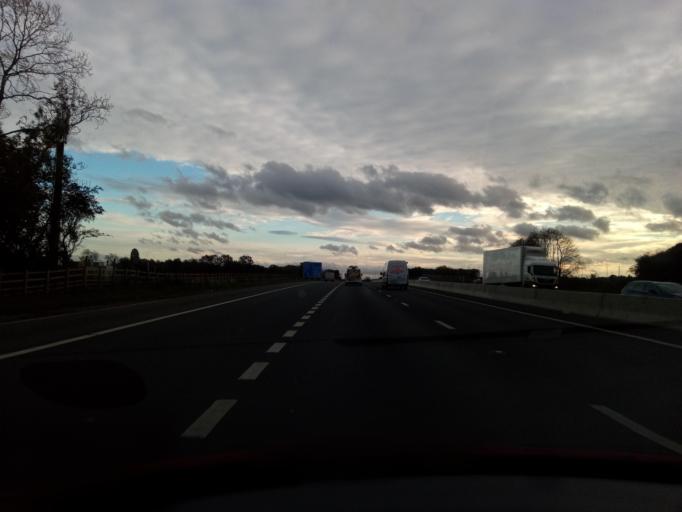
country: GB
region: England
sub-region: North Yorkshire
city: Catterick
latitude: 54.4487
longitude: -1.6683
